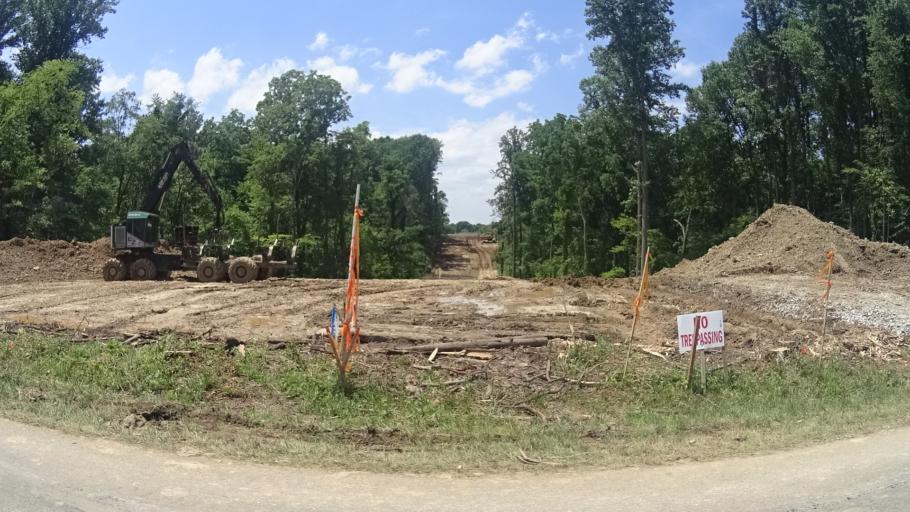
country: US
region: Ohio
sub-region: Erie County
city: Huron
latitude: 41.3372
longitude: -82.5208
